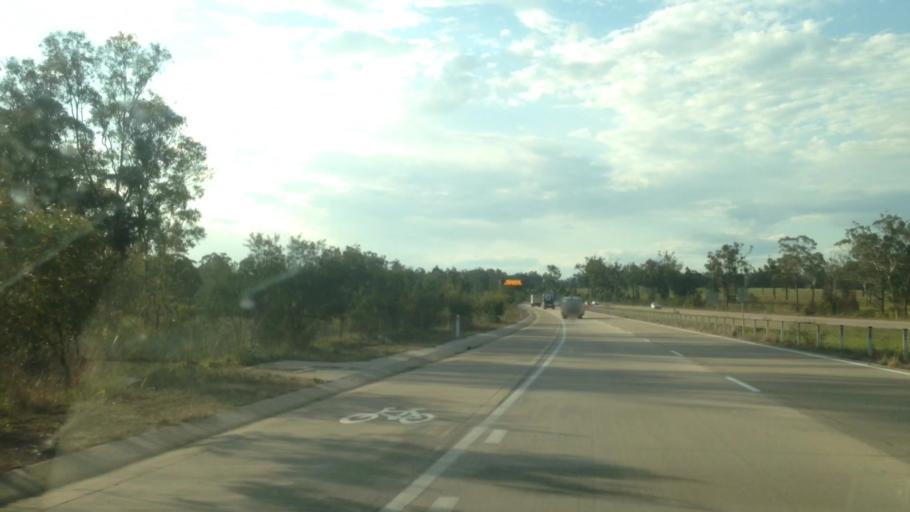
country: AU
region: New South Wales
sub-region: Cessnock
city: Heddon Greta
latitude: -32.8384
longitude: 151.5404
